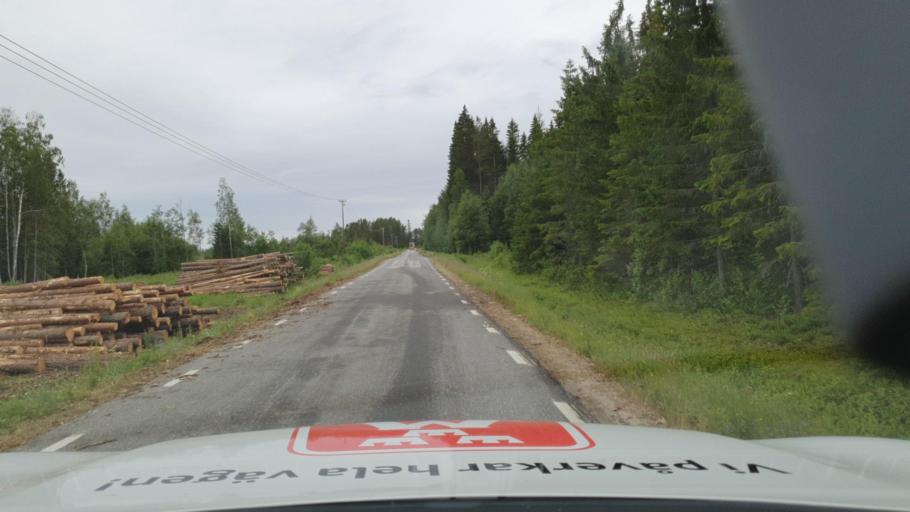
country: SE
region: Vaesterbotten
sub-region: Nordmalings Kommun
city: Nordmaling
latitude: 63.5138
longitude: 19.4212
